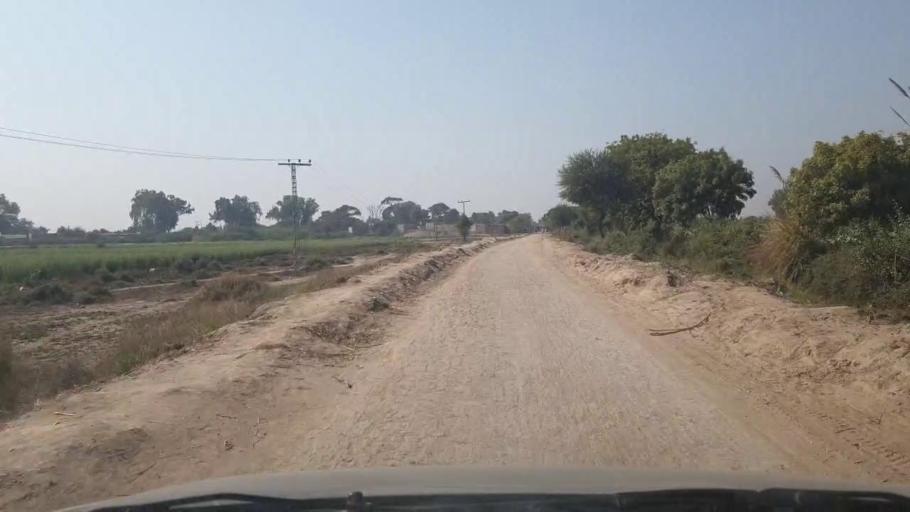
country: PK
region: Sindh
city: Digri
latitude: 25.2334
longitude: 69.0889
